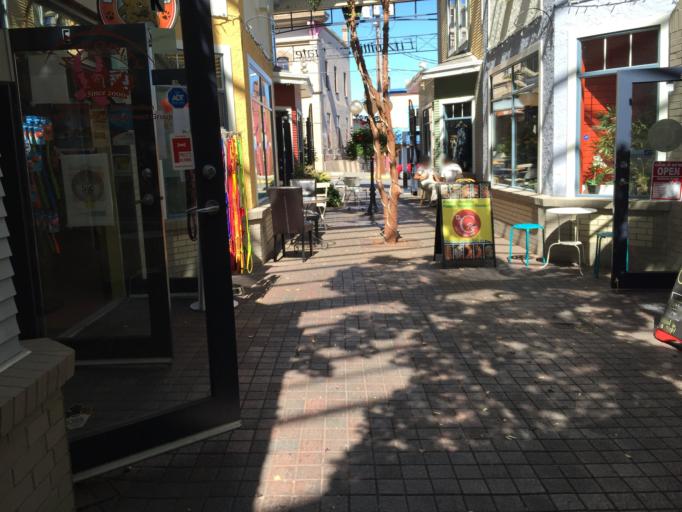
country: CA
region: British Columbia
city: Nanaimo
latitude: 49.1650
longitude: -123.9422
